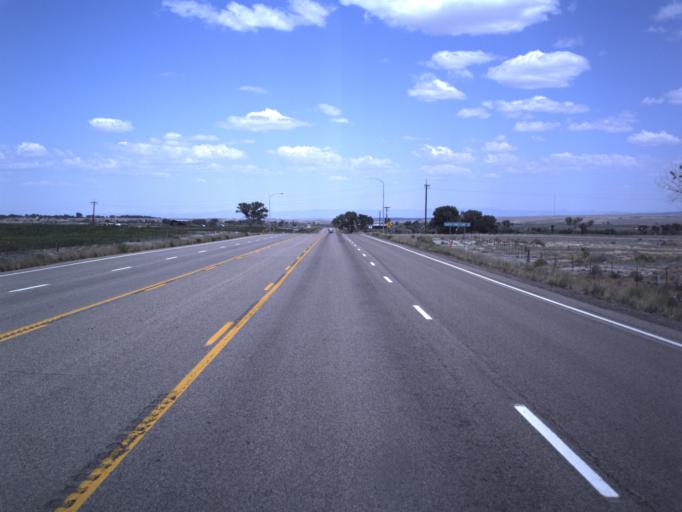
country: US
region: Utah
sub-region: Emery County
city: Castle Dale
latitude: 39.1801
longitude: -111.0410
